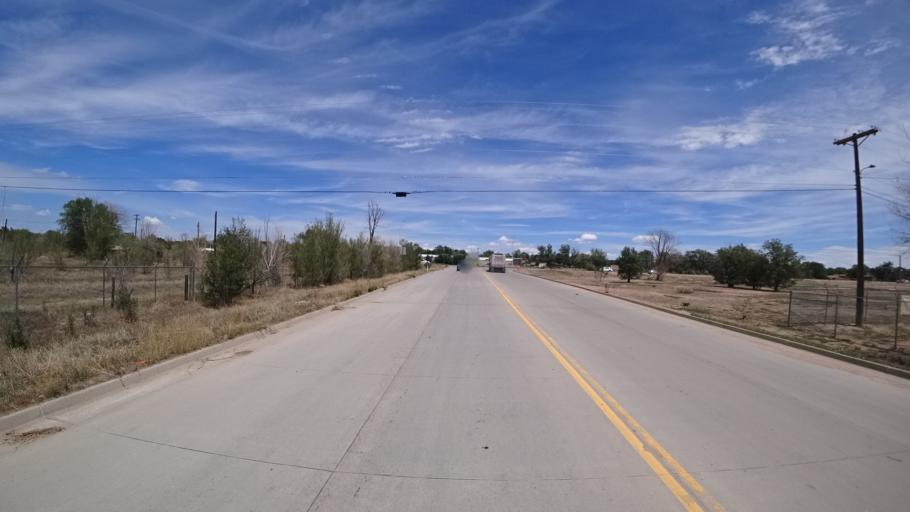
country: US
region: Colorado
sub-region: El Paso County
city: Security-Widefield
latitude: 38.7257
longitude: -104.7222
